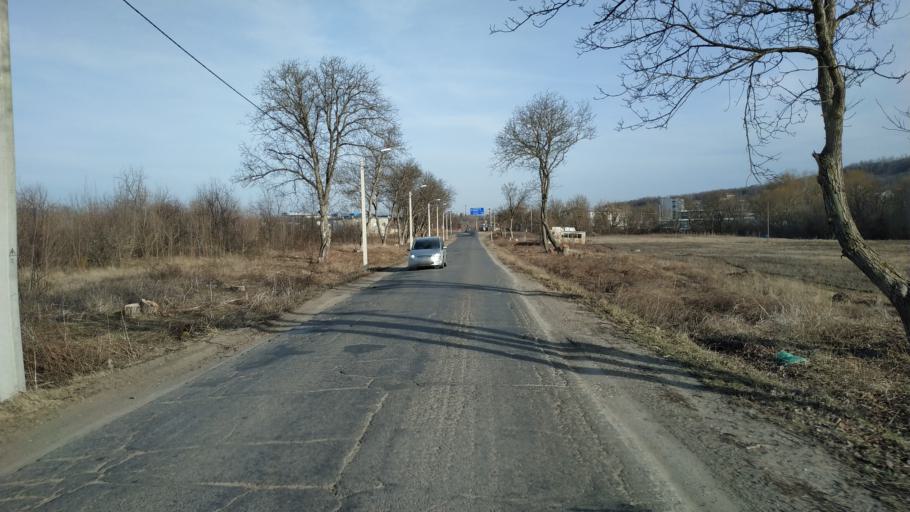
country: MD
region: Chisinau
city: Vatra
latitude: 47.0640
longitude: 28.7404
